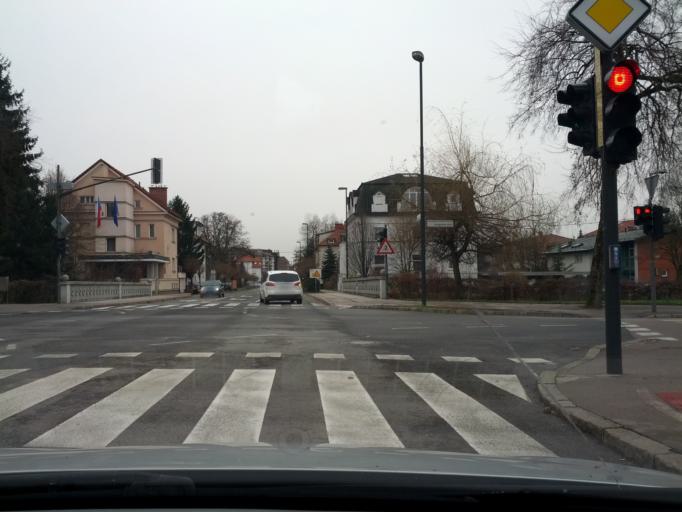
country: SI
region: Ljubljana
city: Ljubljana
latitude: 46.0440
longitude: 14.4974
